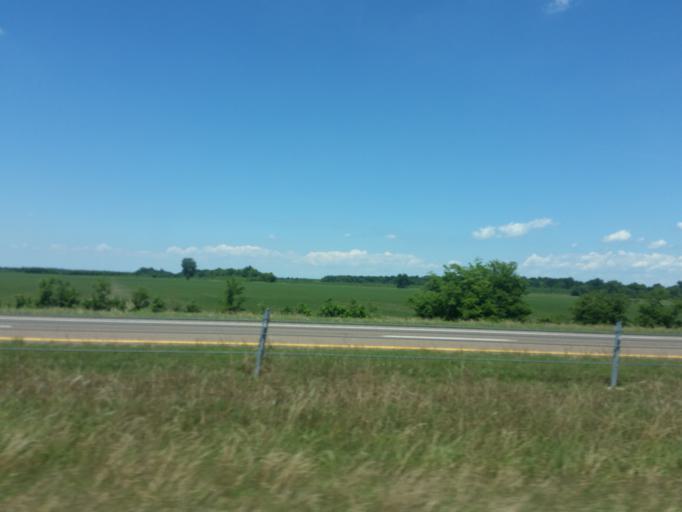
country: US
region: Missouri
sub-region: Pemiscot County
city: Caruthersville
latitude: 36.0861
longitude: -89.5539
